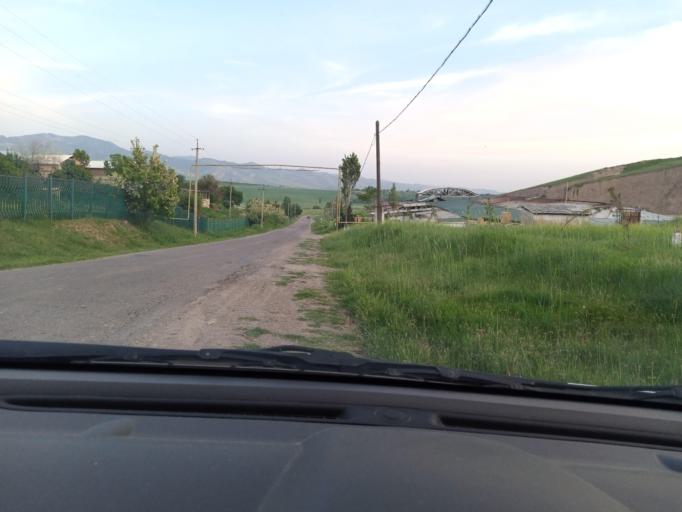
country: UZ
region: Toshkent
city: Parkent
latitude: 41.2335
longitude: 69.7373
